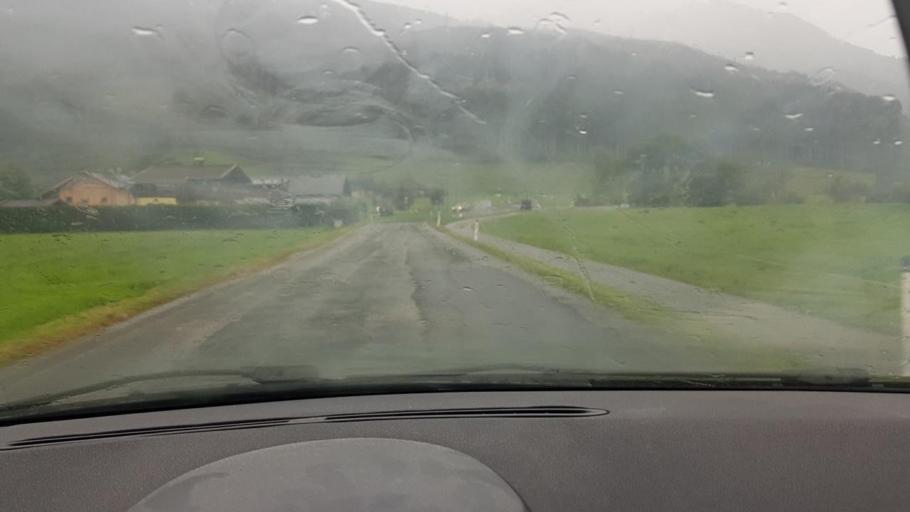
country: AT
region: Salzburg
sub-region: Politischer Bezirk Zell am See
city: Kaprun
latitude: 47.2837
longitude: 12.7839
